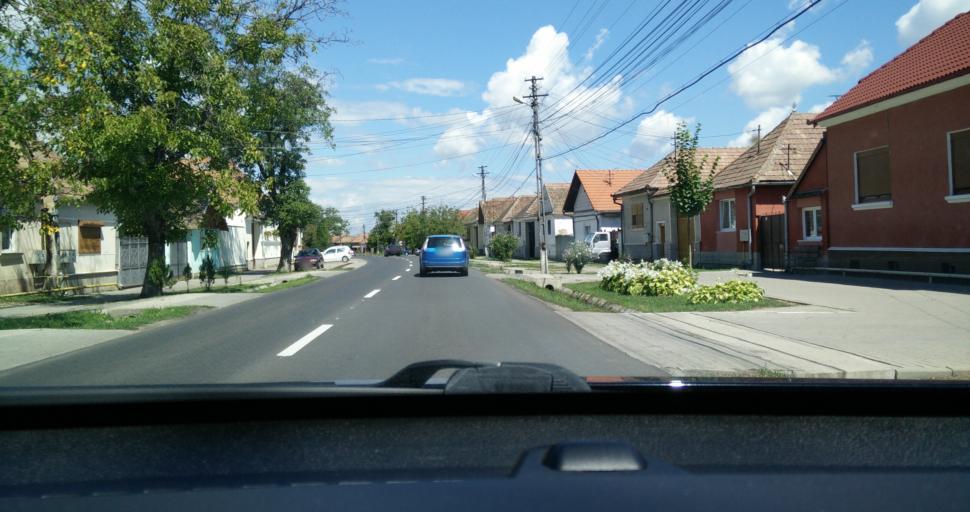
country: RO
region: Alba
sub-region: Municipiul Sebes
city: Petresti
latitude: 45.9223
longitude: 23.5622
